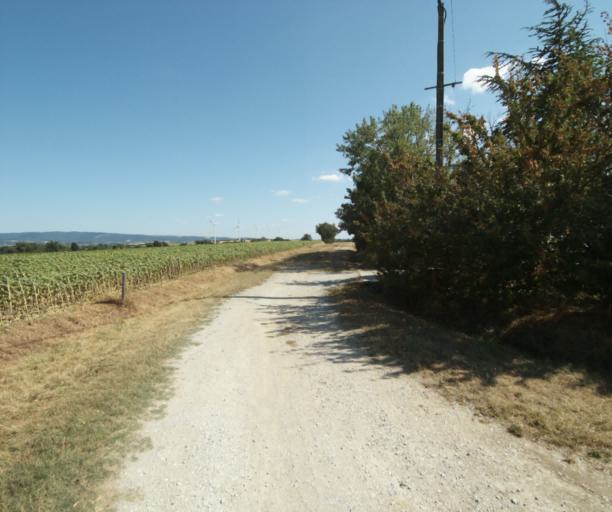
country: FR
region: Midi-Pyrenees
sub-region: Departement de la Haute-Garonne
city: Saint-Felix-Lauragais
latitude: 43.4790
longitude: 1.9084
